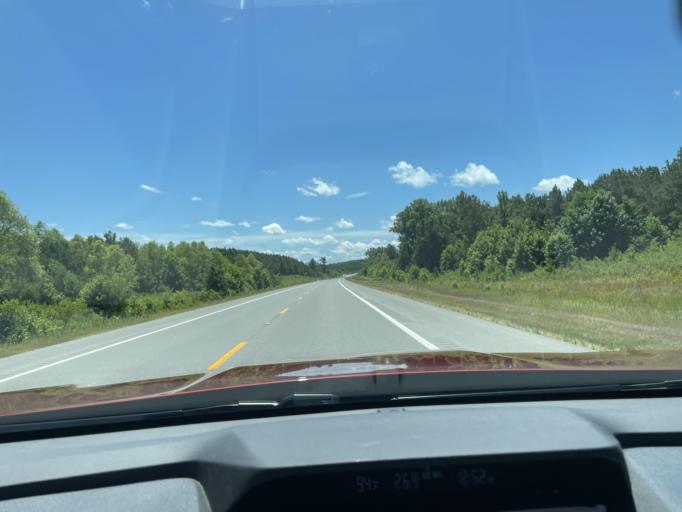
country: US
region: Arkansas
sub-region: Lincoln County
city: Star City
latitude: 33.9269
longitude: -91.8870
